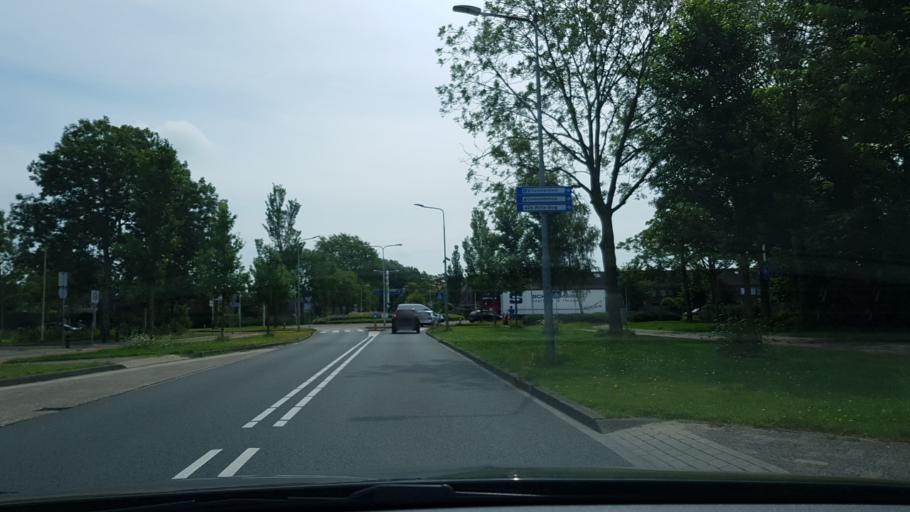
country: NL
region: North Holland
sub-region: Gemeente Castricum
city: Castricum
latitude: 52.5539
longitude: 4.6734
